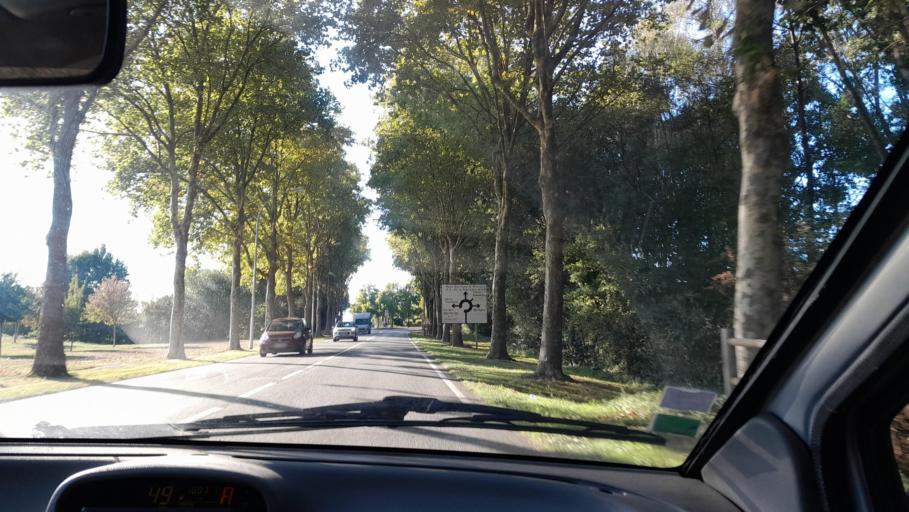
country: FR
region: Pays de la Loire
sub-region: Departement de la Mayenne
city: Craon
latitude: 47.8444
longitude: -0.9622
